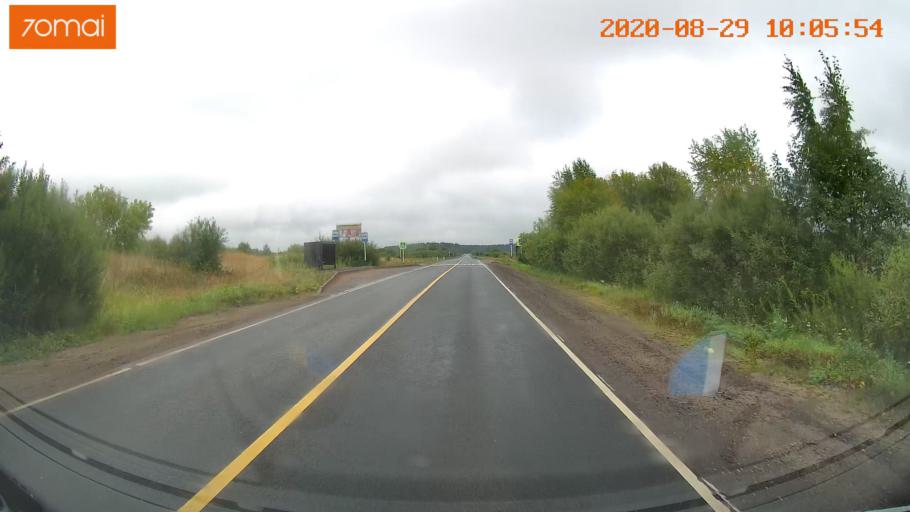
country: RU
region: Ivanovo
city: Zarechnyy
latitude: 57.3912
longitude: 42.5322
